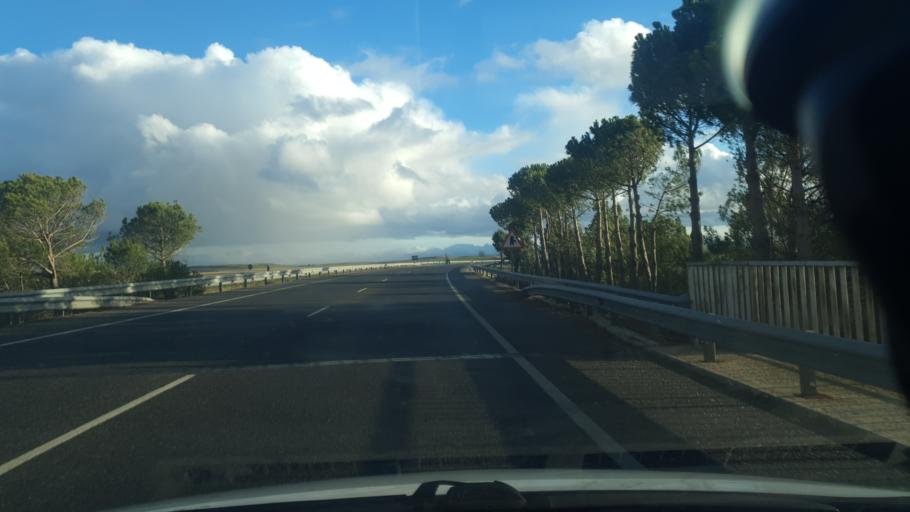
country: ES
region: Castille and Leon
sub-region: Provincia de Segovia
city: Codorniz
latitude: 41.0509
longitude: -4.6248
